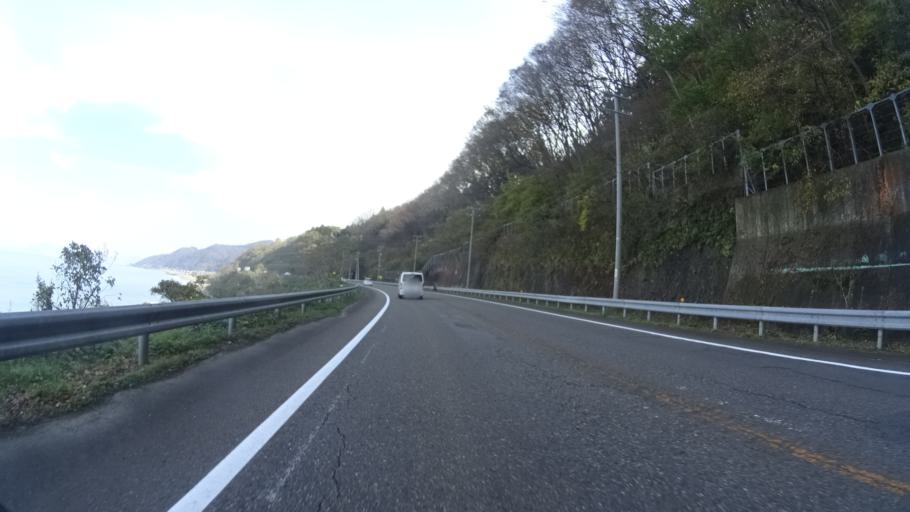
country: JP
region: Niigata
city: Joetsu
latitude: 37.1612
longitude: 138.1495
